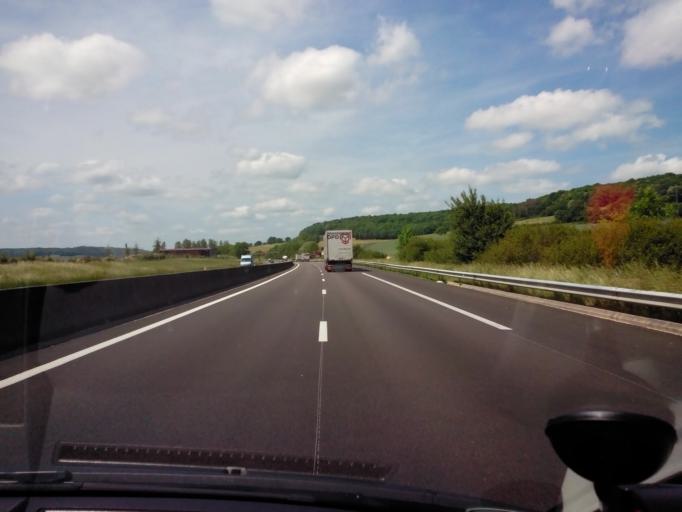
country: FR
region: Champagne-Ardenne
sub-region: Departement de la Haute-Marne
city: Nogent-le-Bas
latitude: 47.9538
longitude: 5.3649
